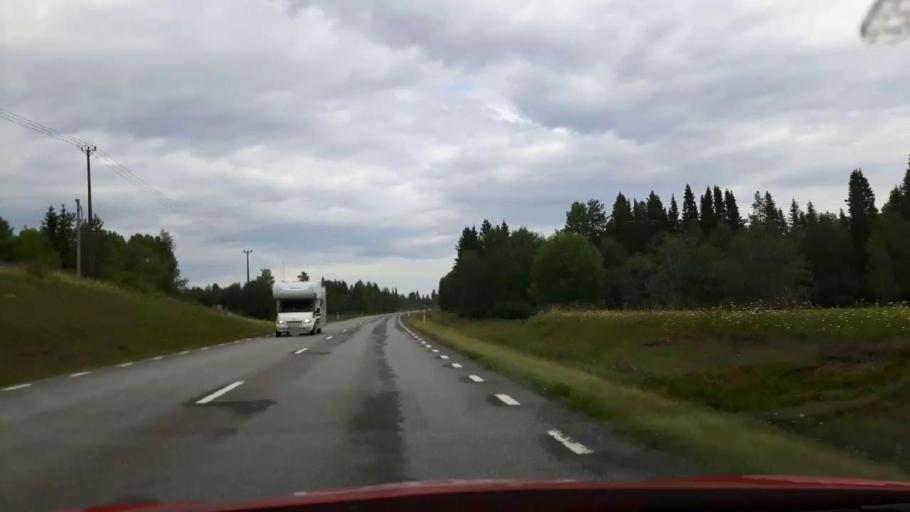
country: SE
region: Jaemtland
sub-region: Stroemsunds Kommun
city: Stroemsund
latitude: 63.6806
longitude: 15.4014
